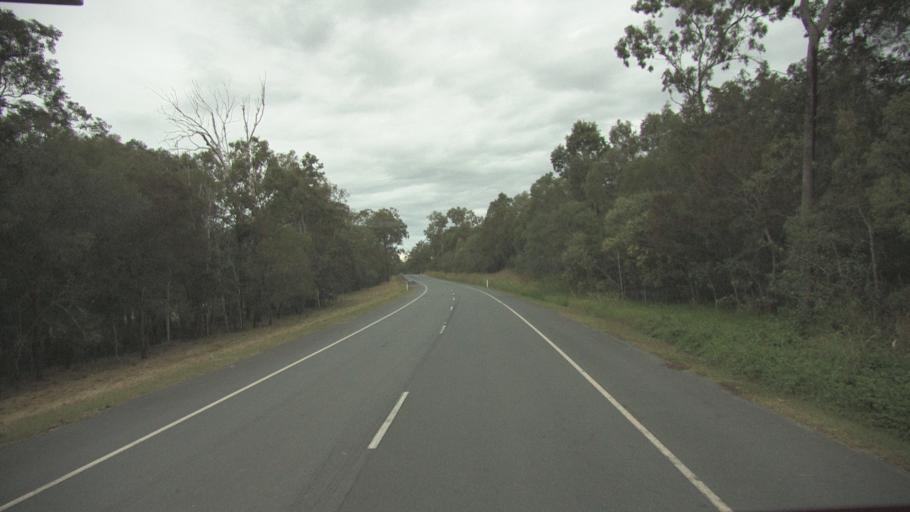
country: AU
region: Queensland
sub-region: Logan
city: Park Ridge South
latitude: -27.7397
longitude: 153.0261
